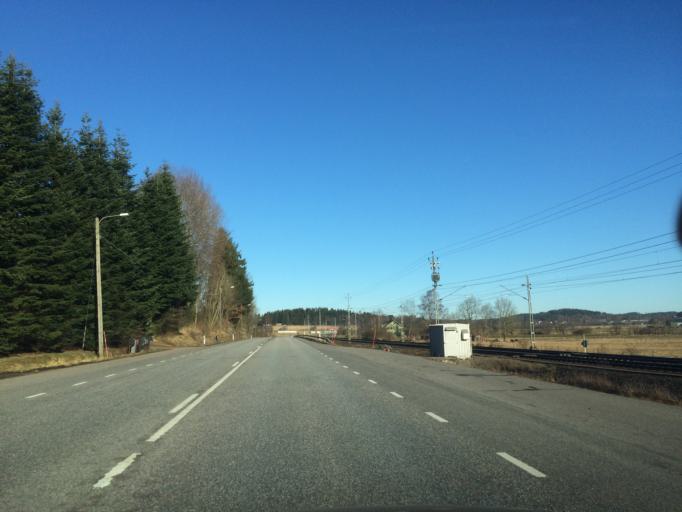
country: SE
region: Vaestra Goetaland
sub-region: Molndal
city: Lindome
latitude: 57.5540
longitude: 12.0905
